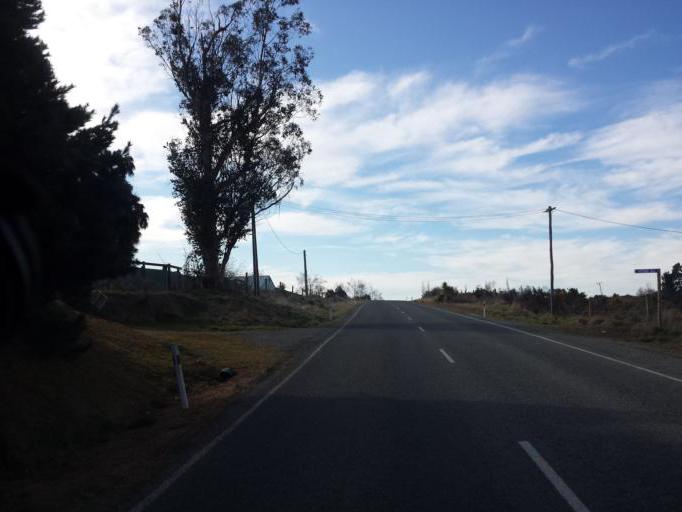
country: NZ
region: Canterbury
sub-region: Timaru District
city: Pleasant Point
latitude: -44.1243
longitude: 171.1033
